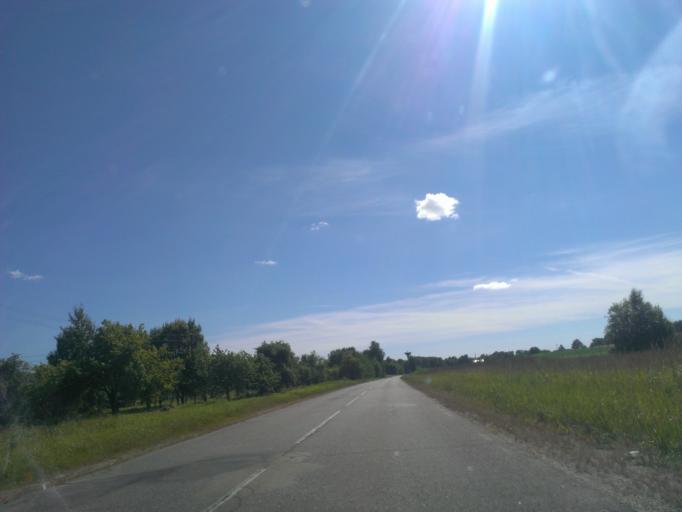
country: LV
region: Malpils
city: Malpils
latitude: 57.0187
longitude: 24.9438
